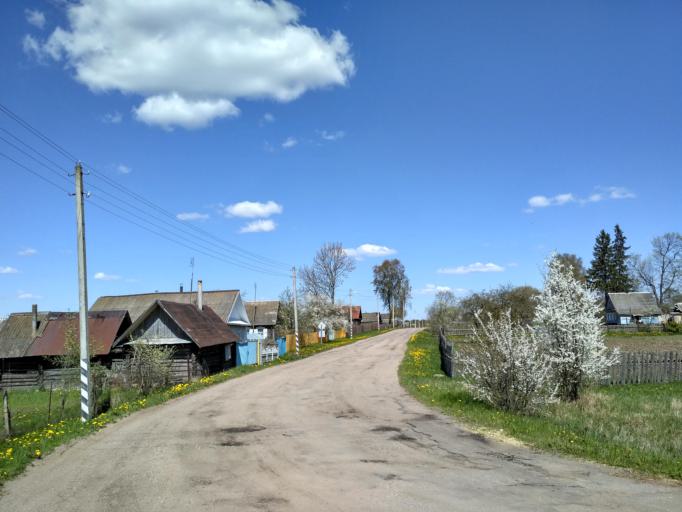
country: BY
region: Minsk
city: Horad Barysaw
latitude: 54.4095
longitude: 28.4561
